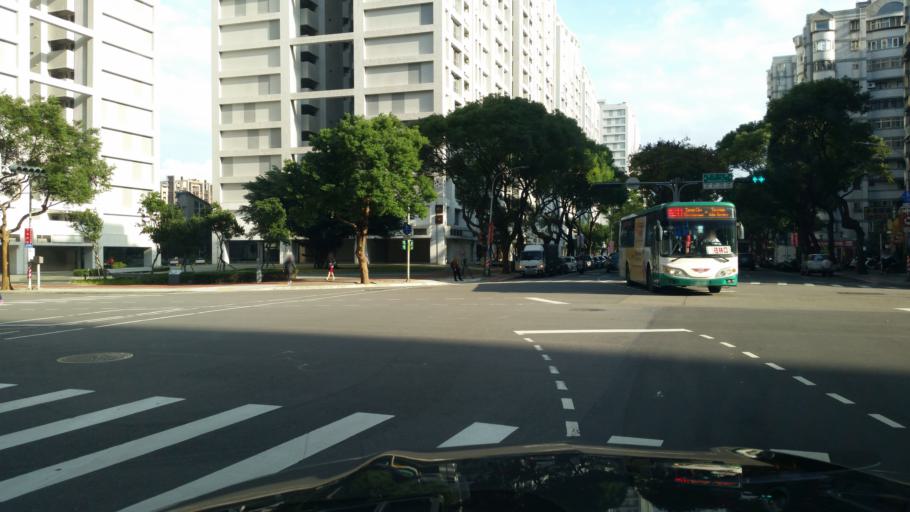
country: TW
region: Taiwan
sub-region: Taoyuan
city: Taoyuan
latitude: 25.0769
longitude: 121.3744
